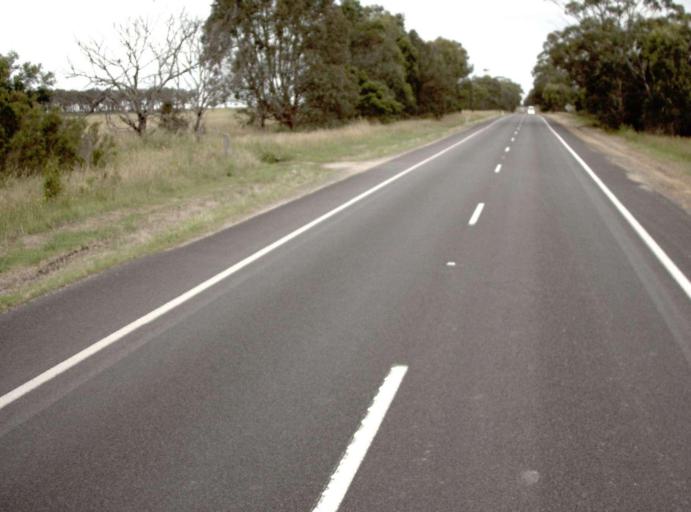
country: AU
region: Victoria
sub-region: Wellington
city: Sale
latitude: -38.2994
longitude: 147.0332
